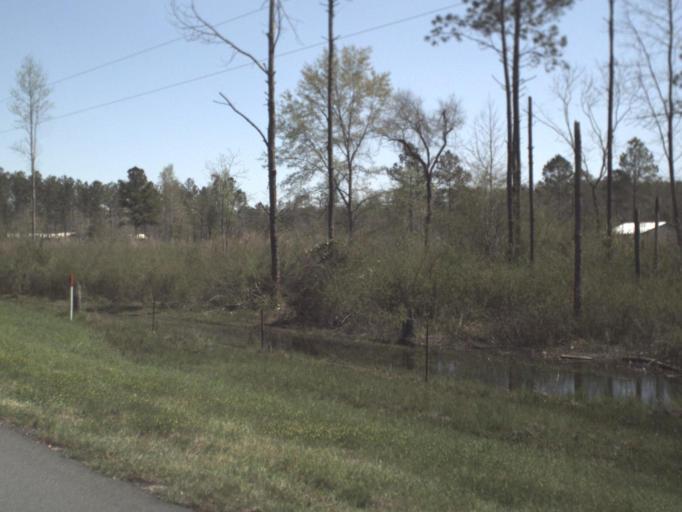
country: US
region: Florida
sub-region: Calhoun County
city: Blountstown
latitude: 30.4370
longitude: -85.2165
